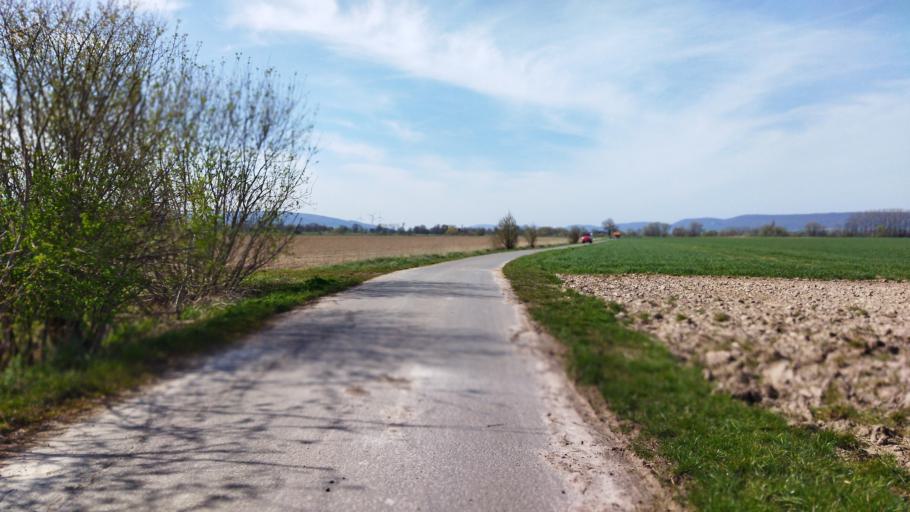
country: DE
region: Lower Saxony
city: Hameln
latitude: 52.1290
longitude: 9.2972
